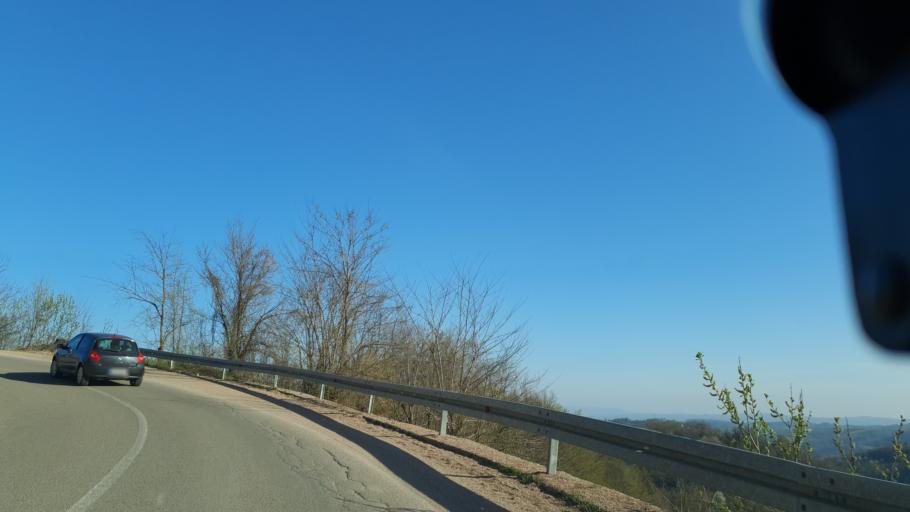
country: RS
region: Central Serbia
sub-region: Kolubarski Okrug
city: Osecina
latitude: 44.2630
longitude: 19.5244
